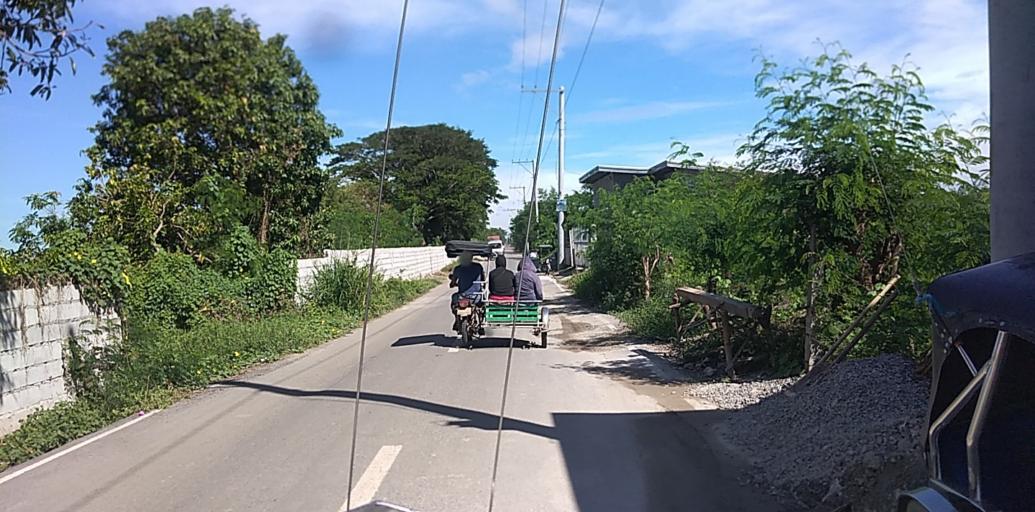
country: PH
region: Central Luzon
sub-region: Province of Pampanga
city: Candaba
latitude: 15.0751
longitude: 120.8073
